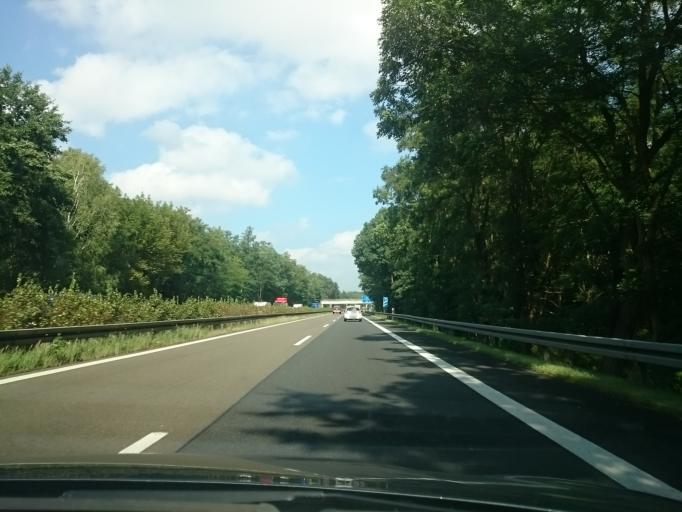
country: DE
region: Brandenburg
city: Marienwerder
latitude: 52.8444
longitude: 13.6649
